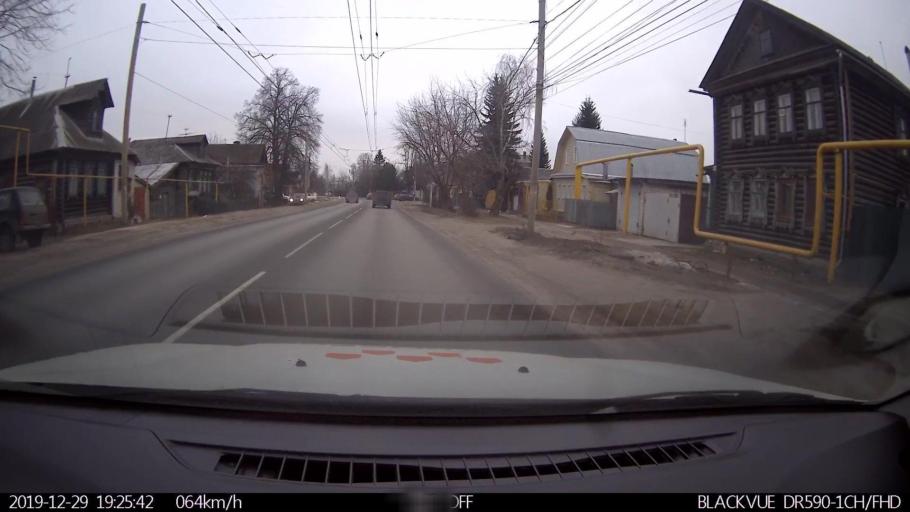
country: RU
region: Nizjnij Novgorod
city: Neklyudovo
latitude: 56.3744
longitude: 43.8356
